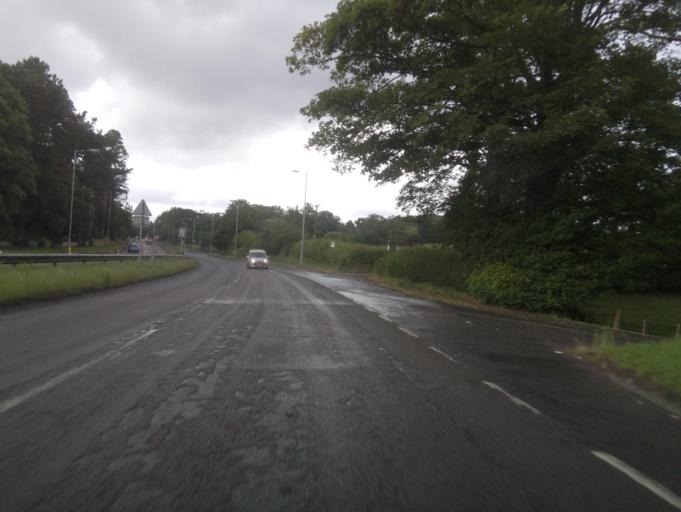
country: GB
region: England
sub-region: Dudley
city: Kingswinford
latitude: 52.5490
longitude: -2.1700
